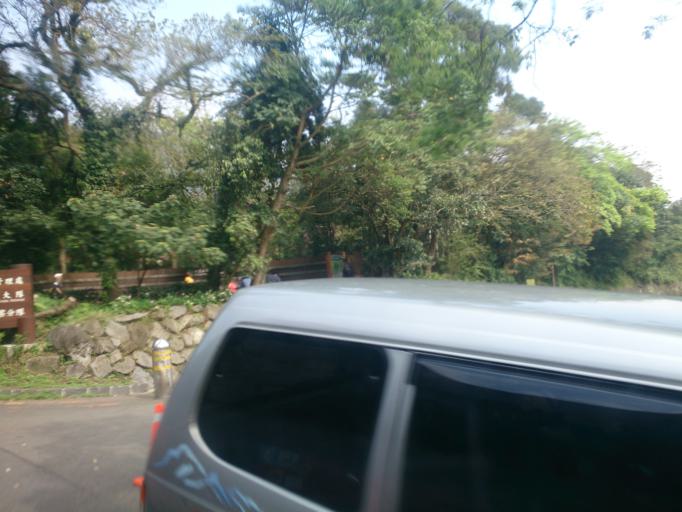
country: TW
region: Taipei
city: Taipei
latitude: 25.1564
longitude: 121.5463
